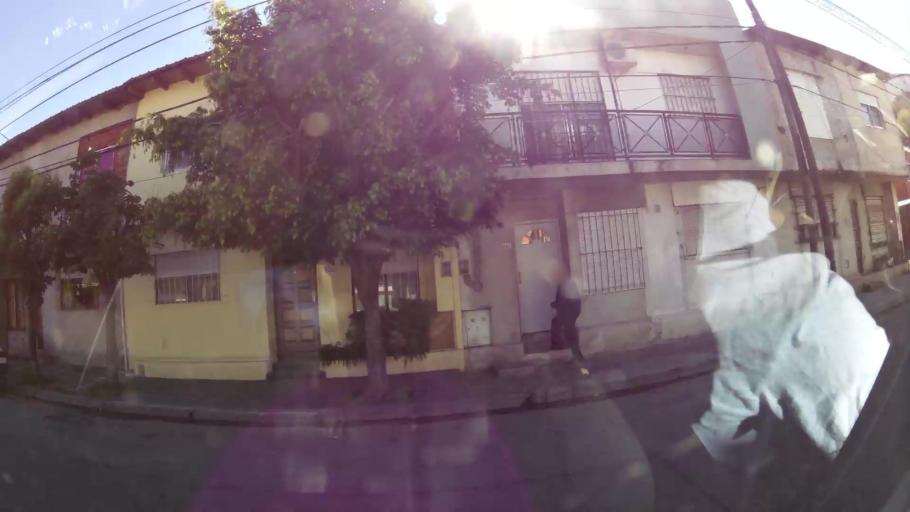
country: AR
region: Buenos Aires
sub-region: Partido de General San Martin
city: General San Martin
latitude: -34.5509
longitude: -58.5276
